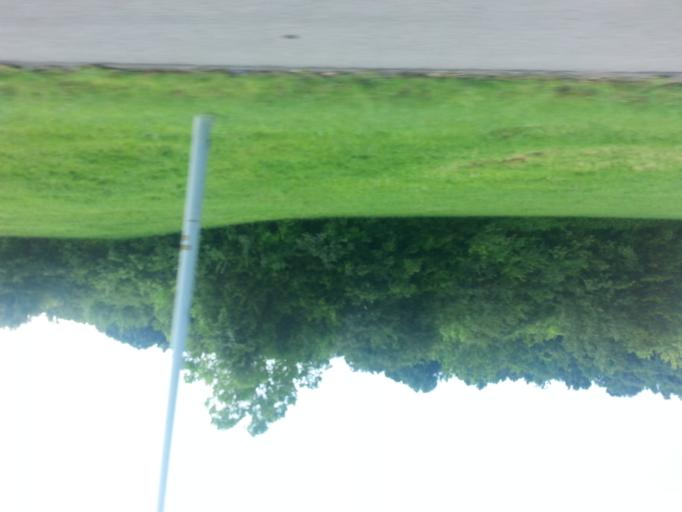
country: US
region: Tennessee
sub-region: Knox County
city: Knoxville
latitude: 36.0293
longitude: -83.8681
